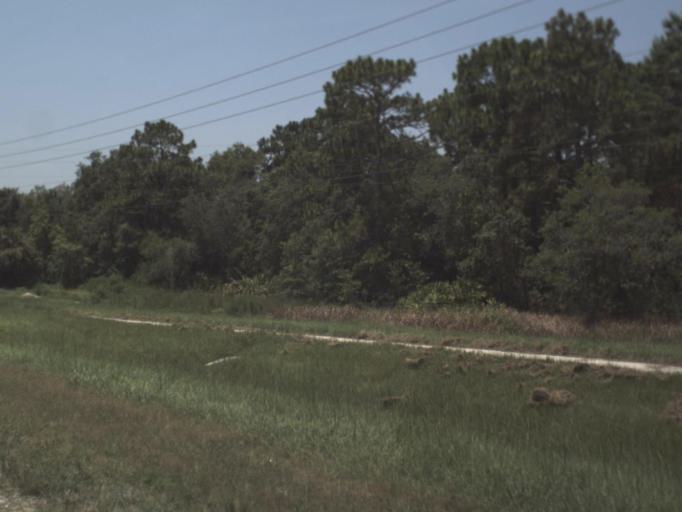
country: US
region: Florida
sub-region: Hernando County
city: North Weeki Wachee
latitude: 28.5413
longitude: -82.5656
